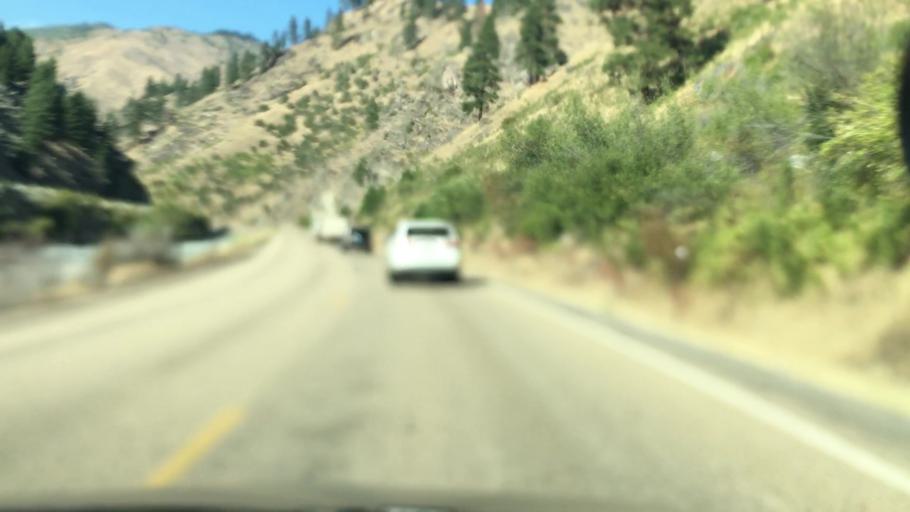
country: US
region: Idaho
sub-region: Boise County
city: Idaho City
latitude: 44.0899
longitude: -116.1062
